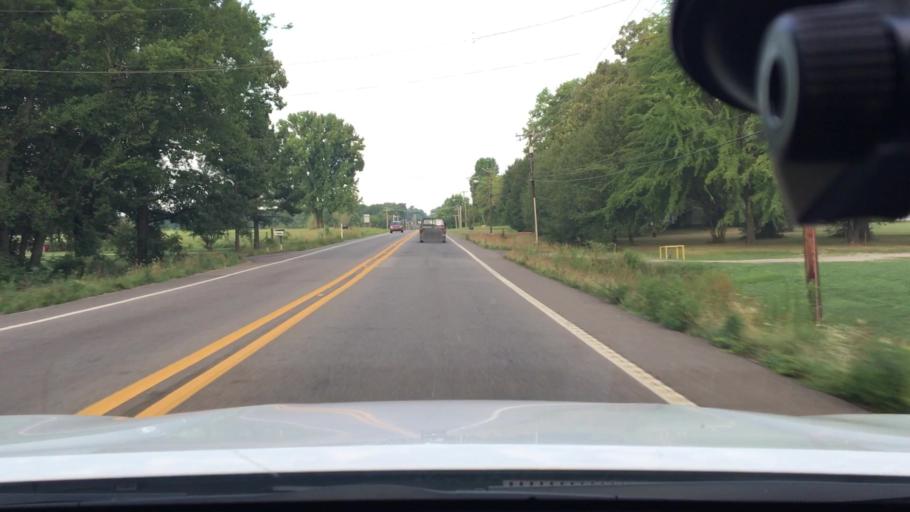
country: US
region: Arkansas
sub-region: Johnson County
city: Clarksville
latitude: 35.4610
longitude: -93.5272
